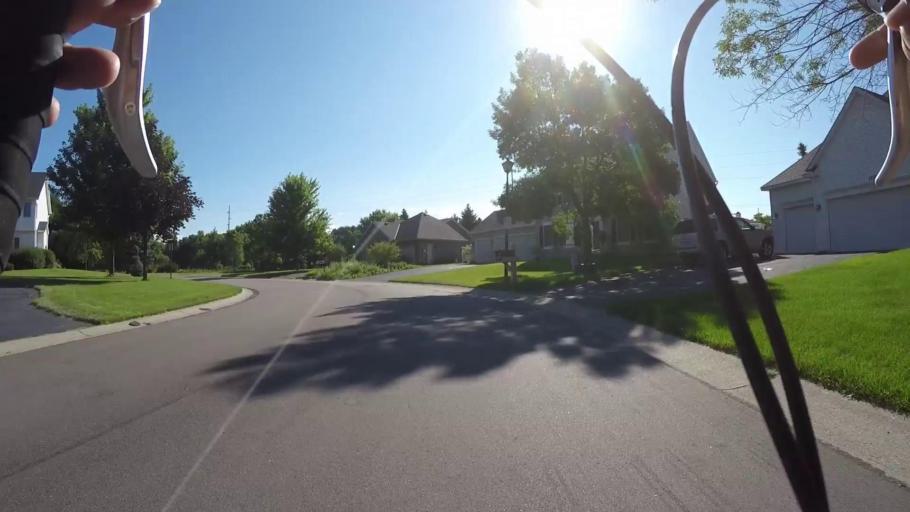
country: US
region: Minnesota
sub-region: Hennepin County
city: Eden Prairie
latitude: 44.8743
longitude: -93.4977
